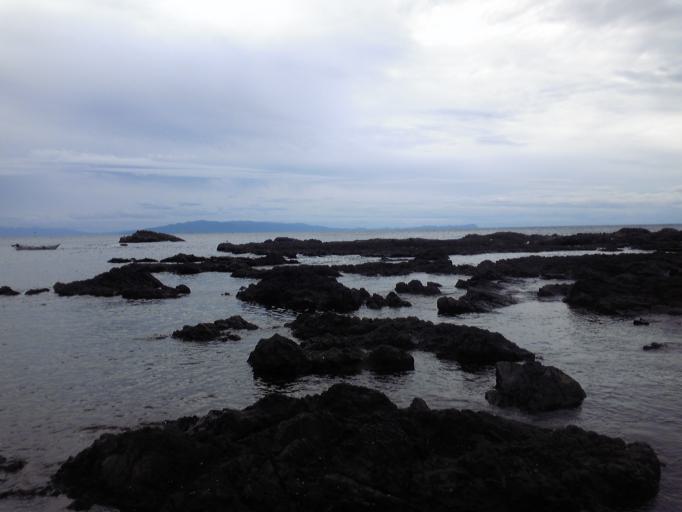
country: JP
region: Aomori
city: Shimokizukuri
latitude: 41.3976
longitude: 140.1972
